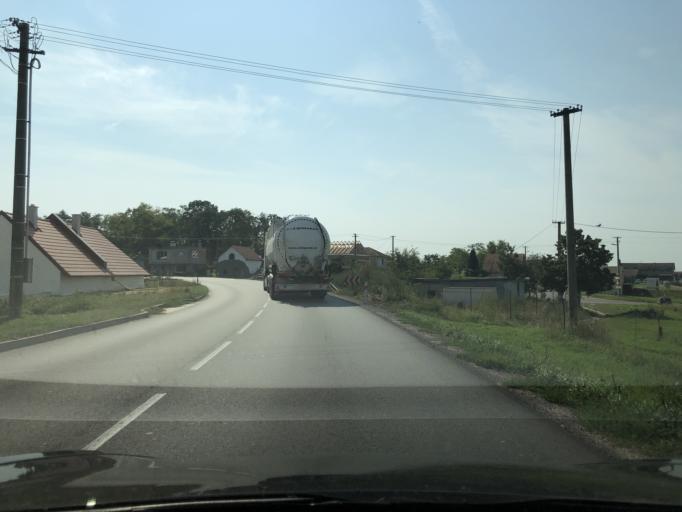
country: CZ
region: South Moravian
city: Novosedly
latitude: 48.8373
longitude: 16.5057
